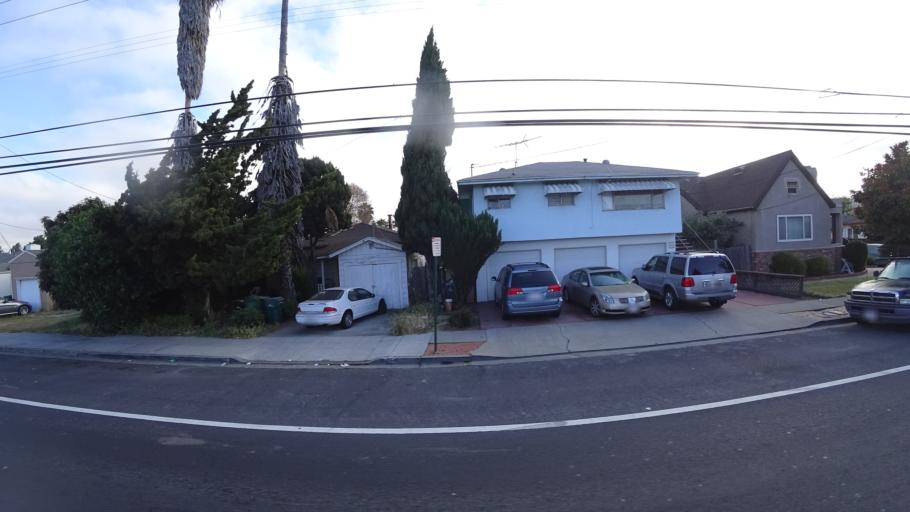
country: US
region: California
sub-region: Alameda County
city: Hayward
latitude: 37.6575
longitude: -122.0848
